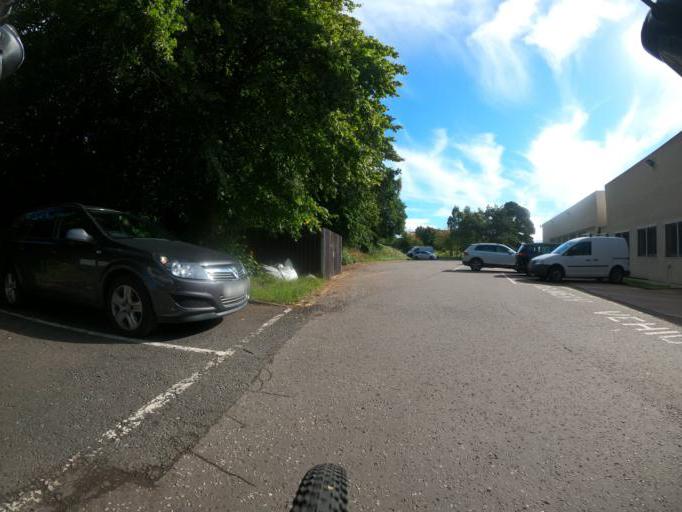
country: GB
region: Scotland
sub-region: Edinburgh
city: Colinton
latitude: 55.9533
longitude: -3.2539
